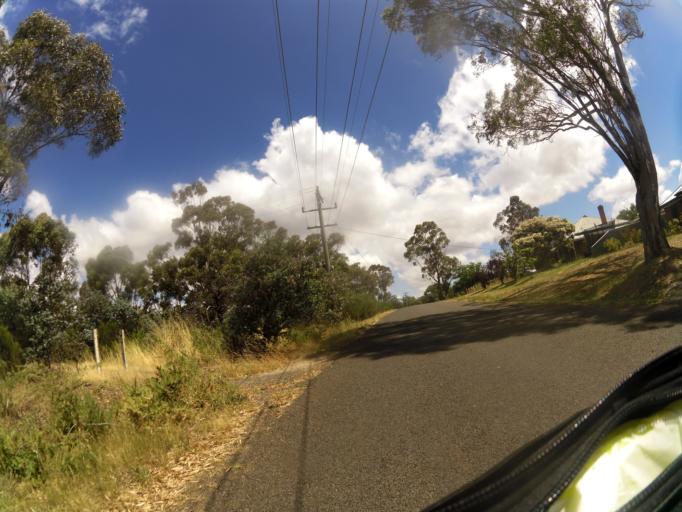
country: AU
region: Victoria
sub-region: Mount Alexander
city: Castlemaine
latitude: -37.0029
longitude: 144.2534
